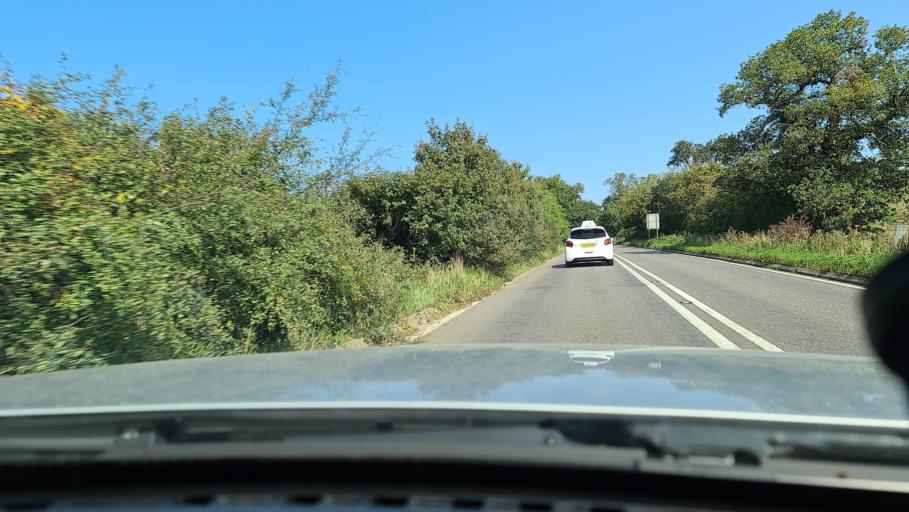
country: GB
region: England
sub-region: Northamptonshire
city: Daventry
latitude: 52.2852
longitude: -1.1695
